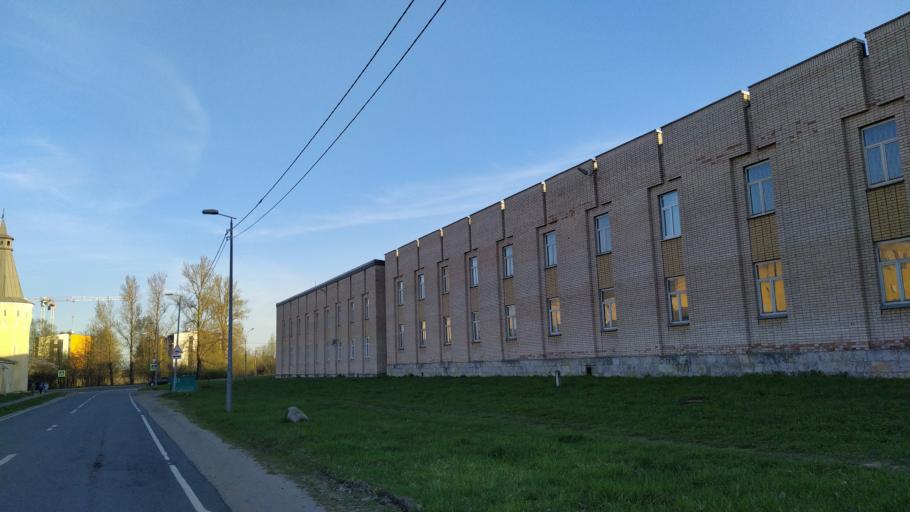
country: RU
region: St.-Petersburg
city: Pushkin
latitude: 59.7026
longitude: 30.3977
